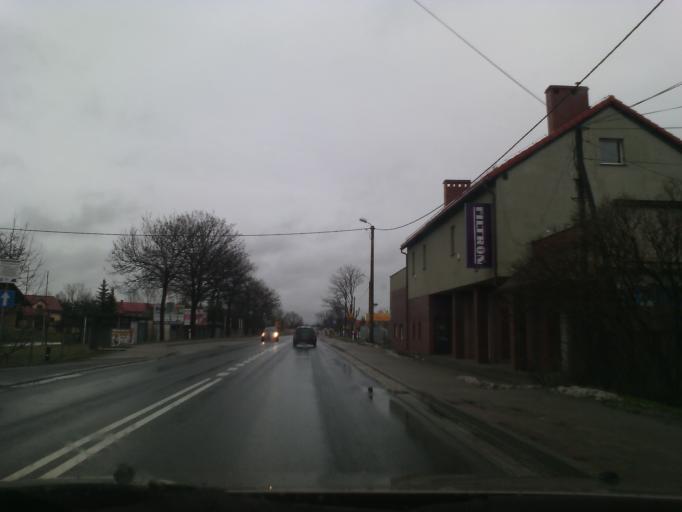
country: PL
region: Lower Silesian Voivodeship
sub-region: Powiat swidnicki
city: Swidnica
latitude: 50.8402
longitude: 16.4388
